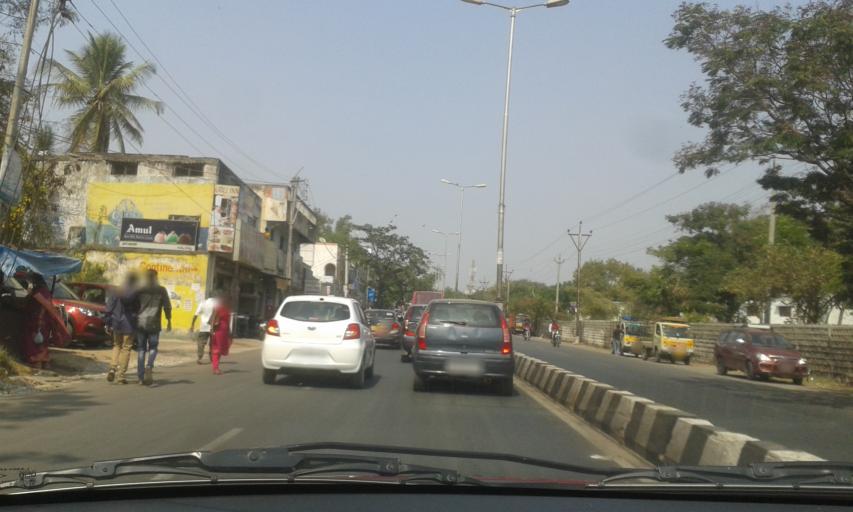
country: IN
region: Telangana
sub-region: Rangareddi
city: Secunderabad
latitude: 17.4995
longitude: 78.5136
